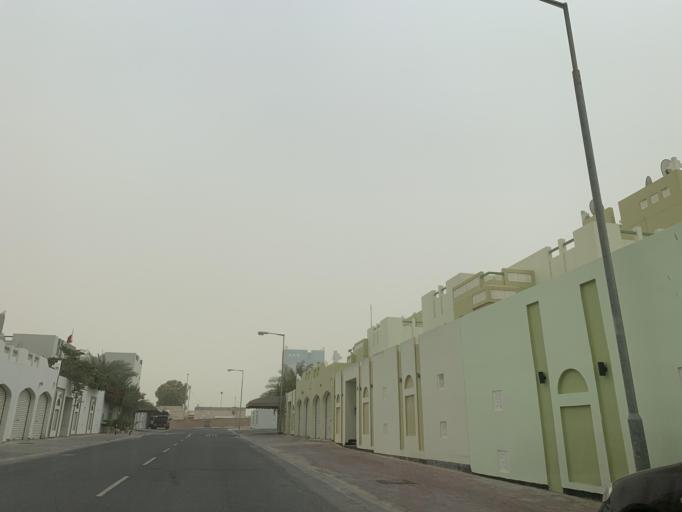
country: BH
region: Central Governorate
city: Madinat Hamad
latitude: 26.1271
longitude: 50.5102
